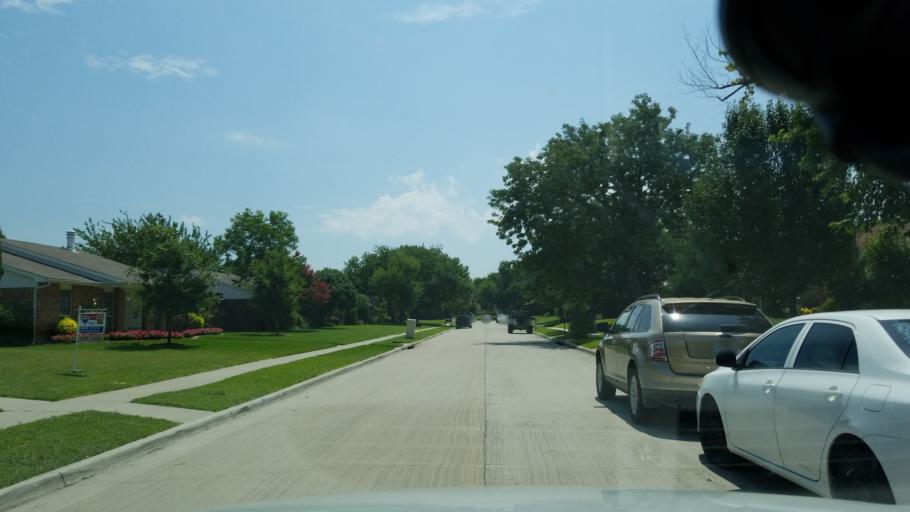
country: US
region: Texas
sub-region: Dallas County
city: Coppell
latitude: 32.9650
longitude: -96.9865
